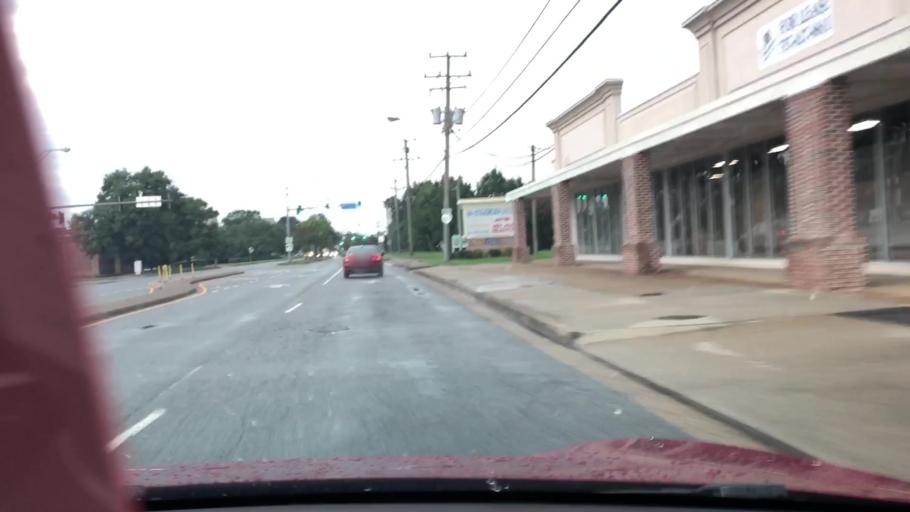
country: US
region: Virginia
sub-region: City of Chesapeake
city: Chesapeake
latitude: 36.8545
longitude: -76.1940
